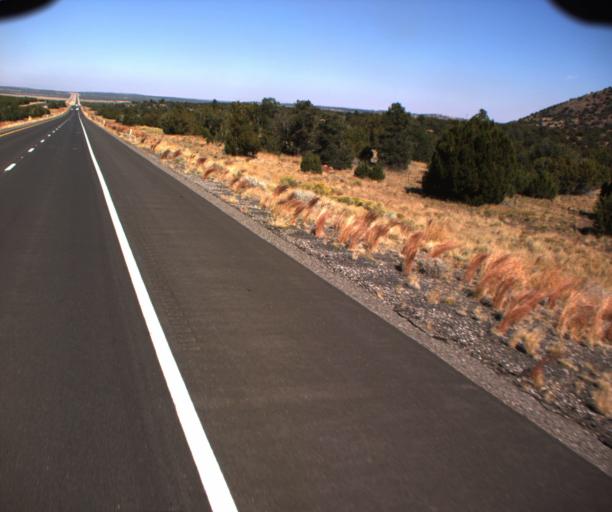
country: US
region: Arizona
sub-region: Coconino County
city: Flagstaff
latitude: 35.4099
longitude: -111.5734
